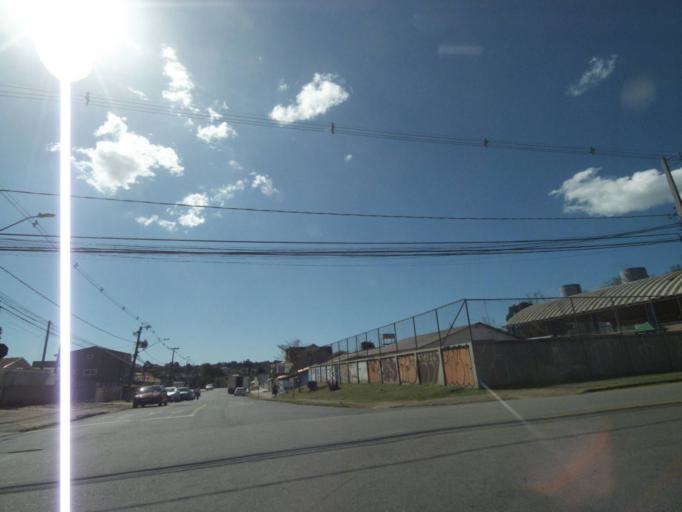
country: BR
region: Parana
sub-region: Curitiba
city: Curitiba
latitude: -25.3801
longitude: -49.2461
